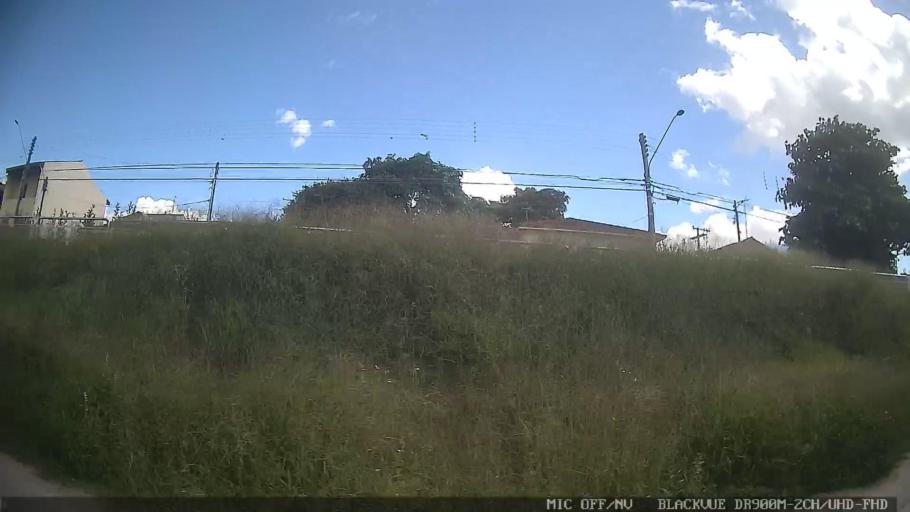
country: BR
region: Sao Paulo
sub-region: Atibaia
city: Atibaia
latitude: -23.1102
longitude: -46.5388
